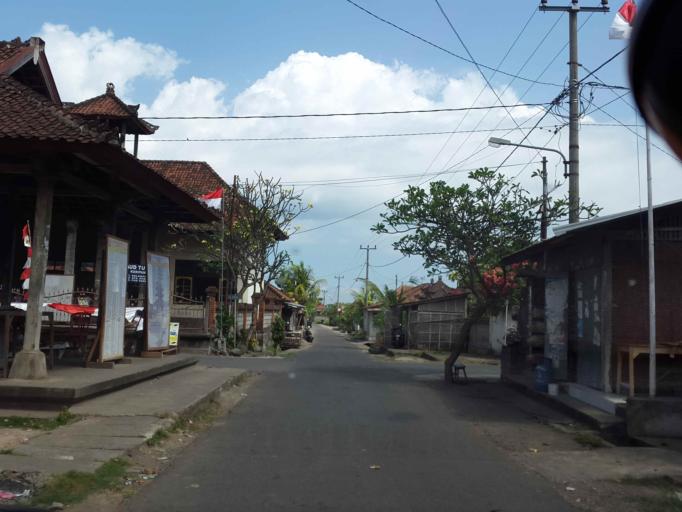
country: ID
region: Bali
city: Klungkung
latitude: -8.5518
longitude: 115.3786
